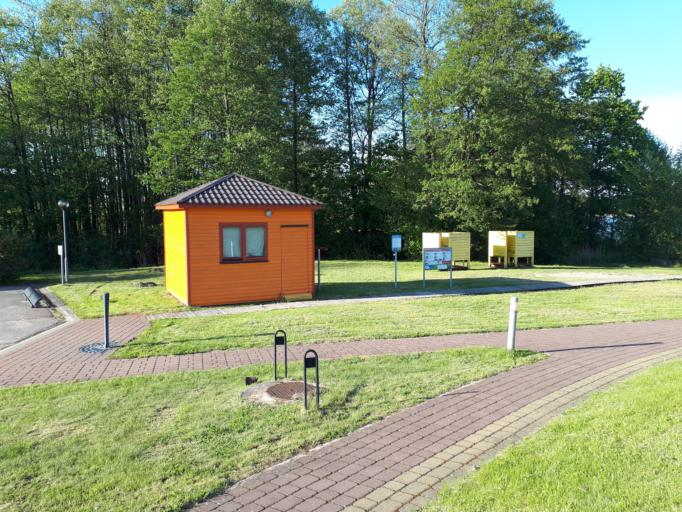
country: LT
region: Alytaus apskritis
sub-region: Alytaus rajonas
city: Daugai
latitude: 54.4669
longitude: 24.3850
